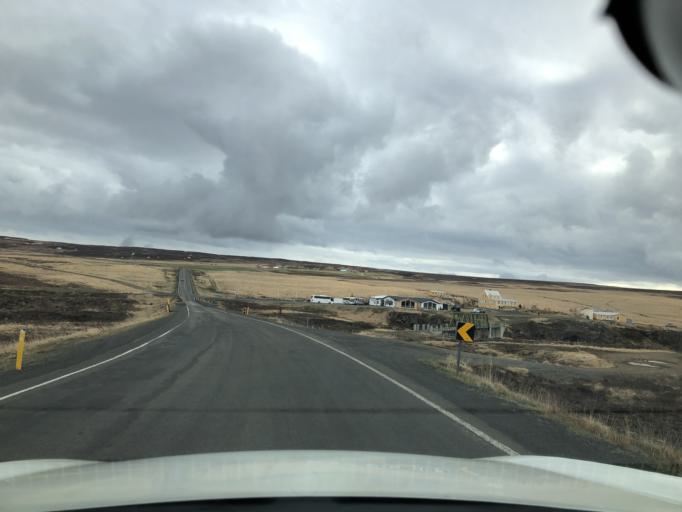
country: IS
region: Northeast
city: Laugar
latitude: 65.6867
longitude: -17.5444
